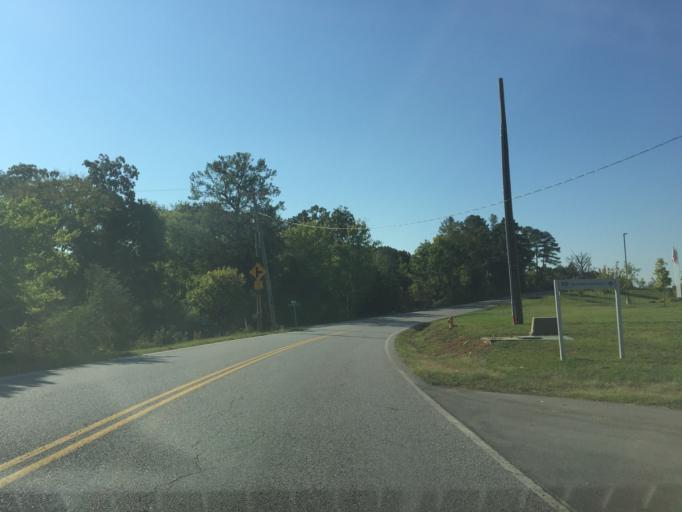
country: US
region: Tennessee
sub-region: Hamilton County
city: Harrison
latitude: 35.0816
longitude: -85.1523
